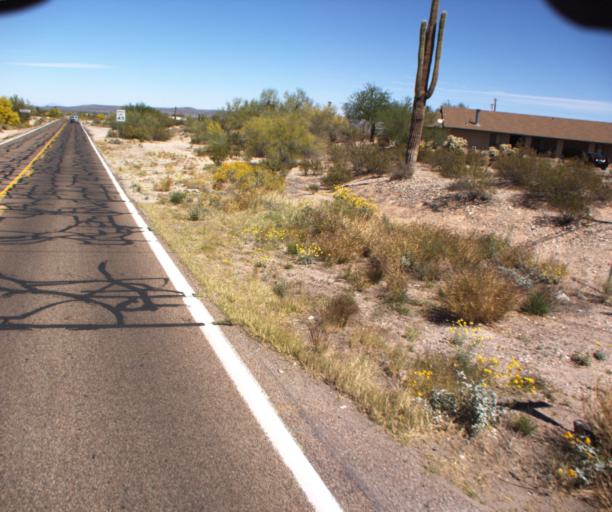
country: US
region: Arizona
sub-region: Pima County
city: Ajo
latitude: 32.3965
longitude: -112.8721
